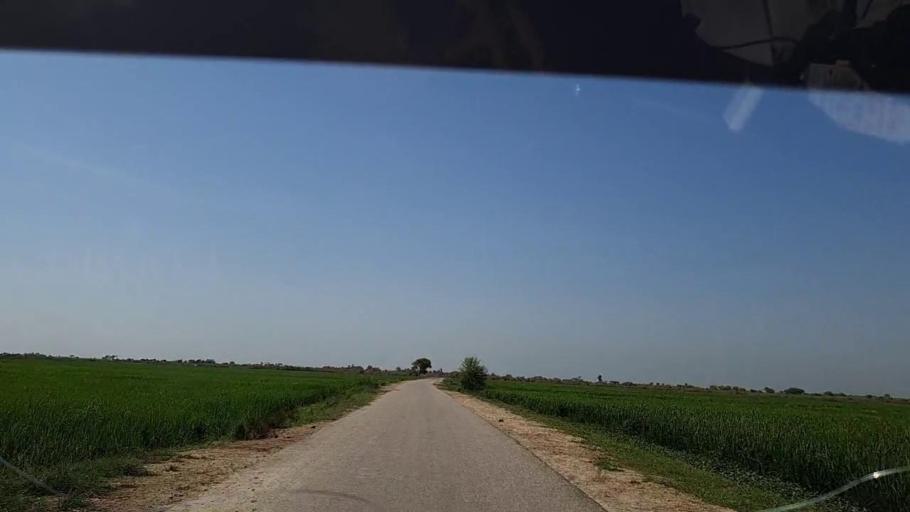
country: PK
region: Sindh
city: Kandhkot
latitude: 28.3112
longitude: 69.1019
